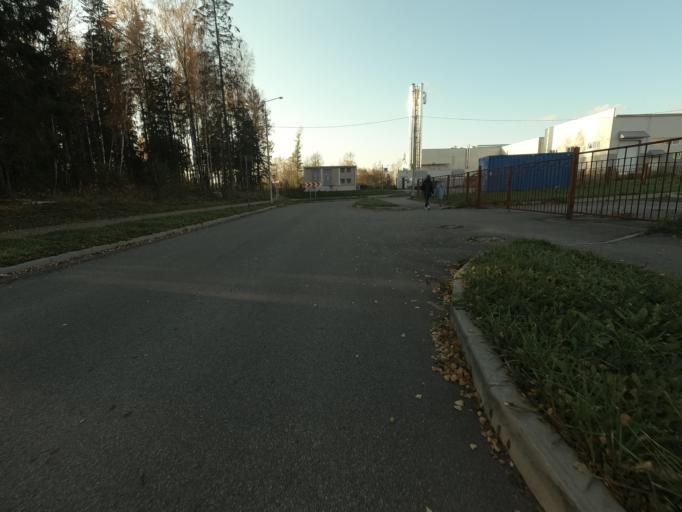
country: RU
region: Leningrad
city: Sertolovo
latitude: 60.1647
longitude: 30.1860
